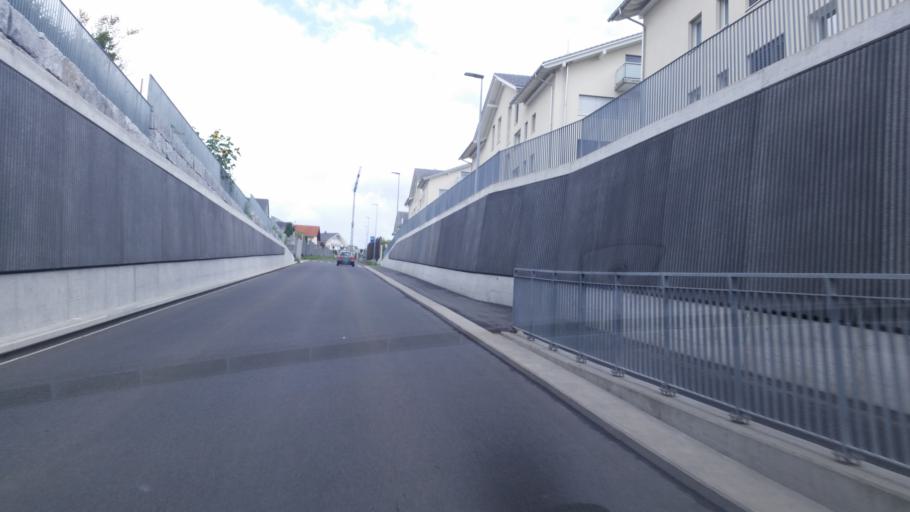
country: CH
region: Schwyz
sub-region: Bezirk Einsiedeln
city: Einsiedeln
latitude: 47.1352
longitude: 8.7475
